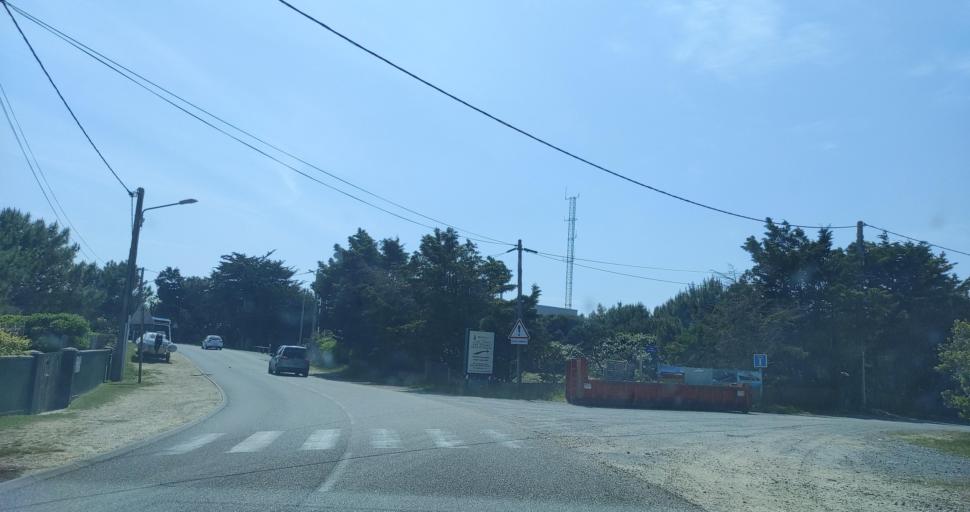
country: FR
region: Aquitaine
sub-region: Departement de la Gironde
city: Arcachon
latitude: 44.6471
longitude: -1.2541
